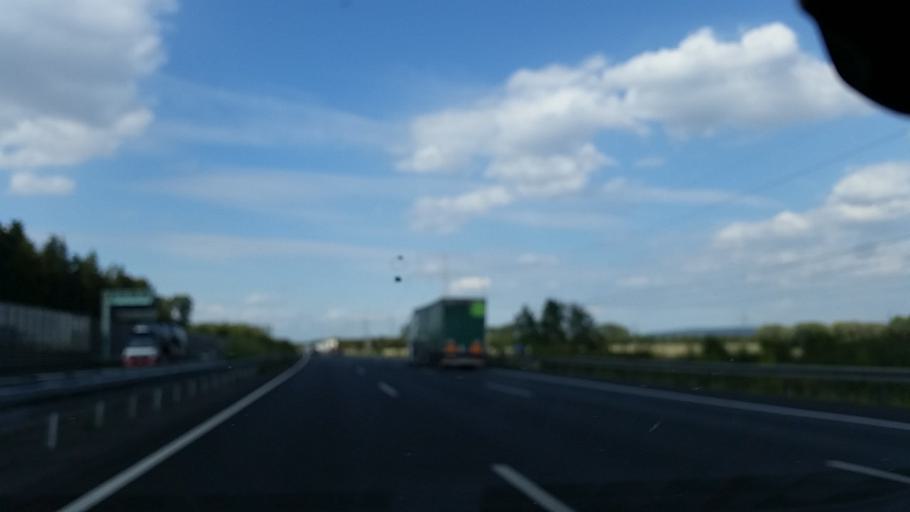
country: DE
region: Lower Saxony
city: Rosdorf
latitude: 51.4971
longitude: 9.8779
